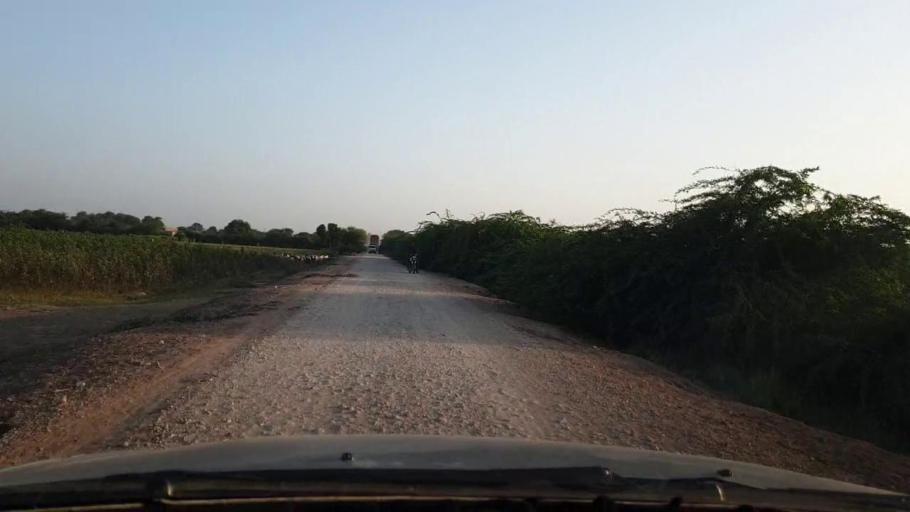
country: PK
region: Sindh
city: Tando Ghulam Ali
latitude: 25.1045
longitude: 68.9387
